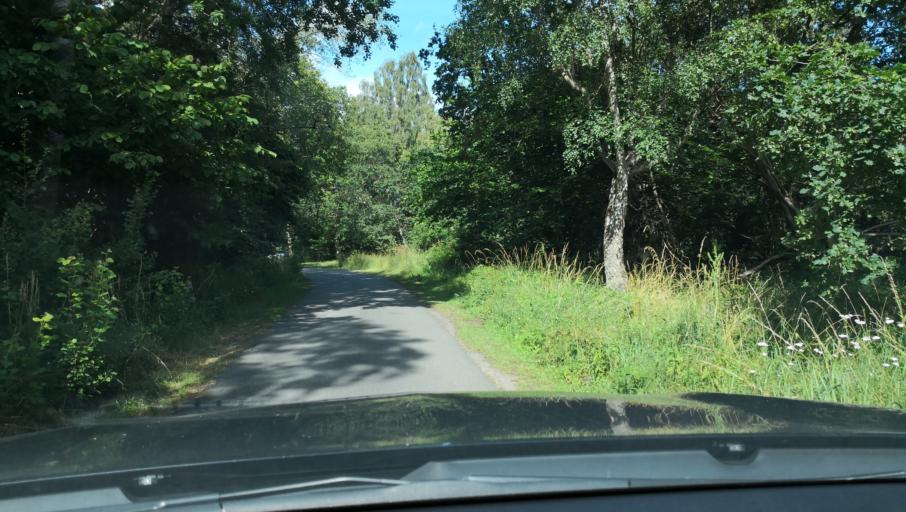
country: SE
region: Skane
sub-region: Ystads Kommun
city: Kopingebro
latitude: 55.3829
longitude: 14.1447
